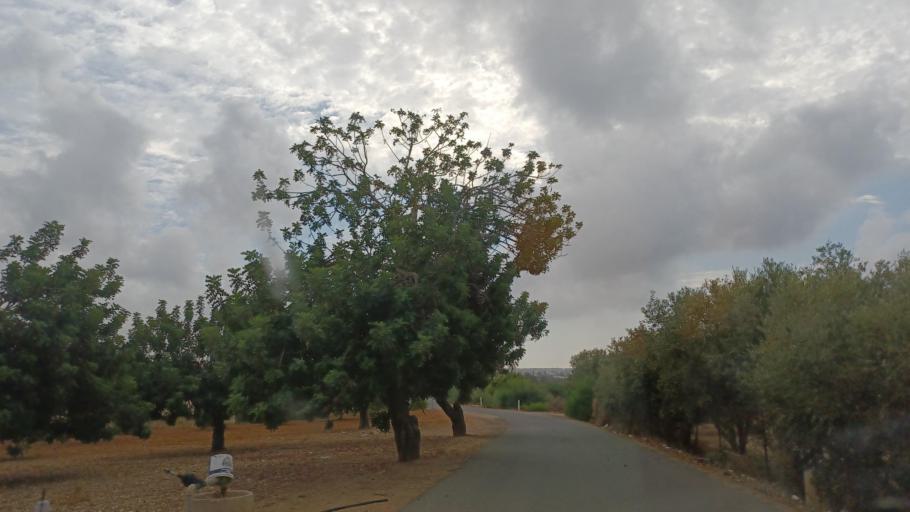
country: CY
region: Pafos
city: Tala
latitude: 34.8254
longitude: 32.4208
